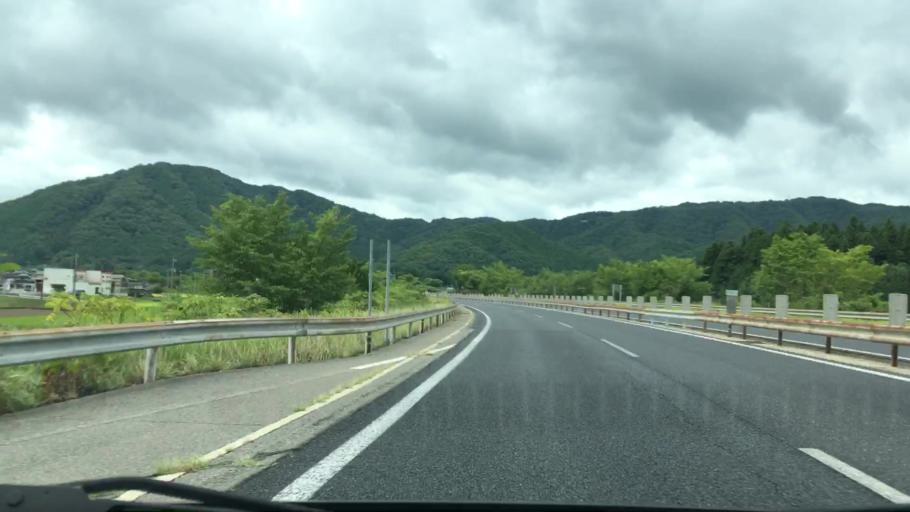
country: JP
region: Okayama
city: Takahashi
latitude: 34.9913
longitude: 133.6970
